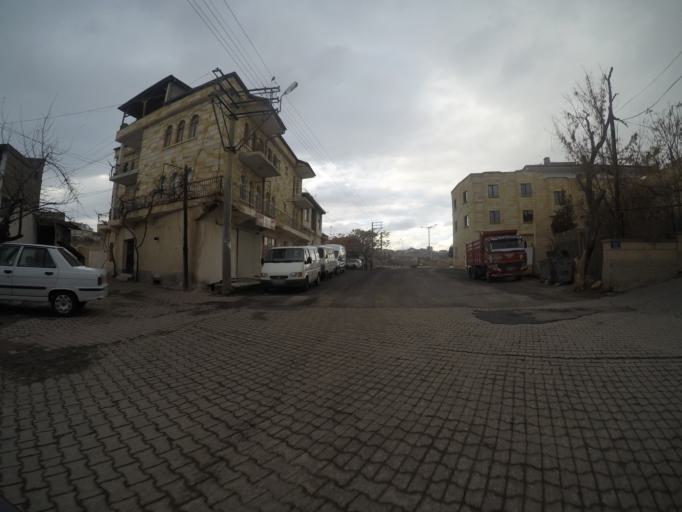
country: TR
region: Nevsehir
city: Goereme
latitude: 38.6237
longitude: 34.8627
